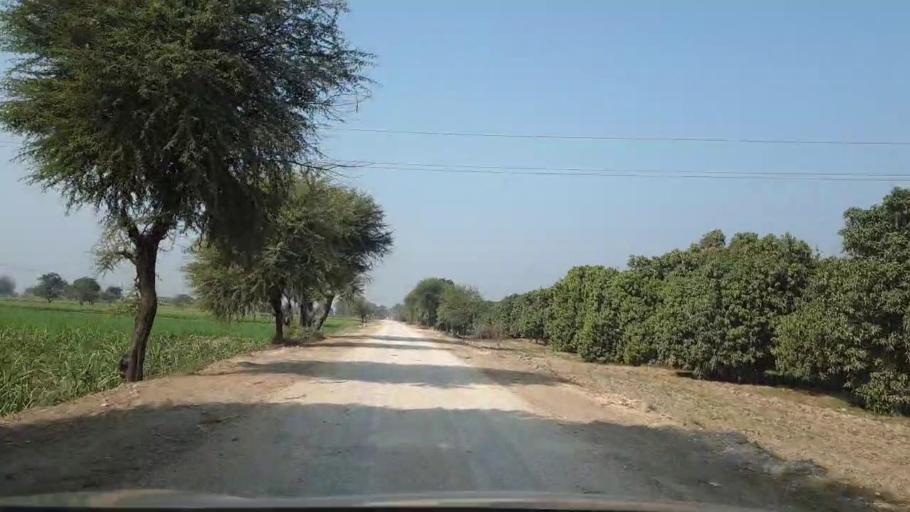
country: PK
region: Sindh
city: Tando Allahyar
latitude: 25.5121
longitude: 68.7700
